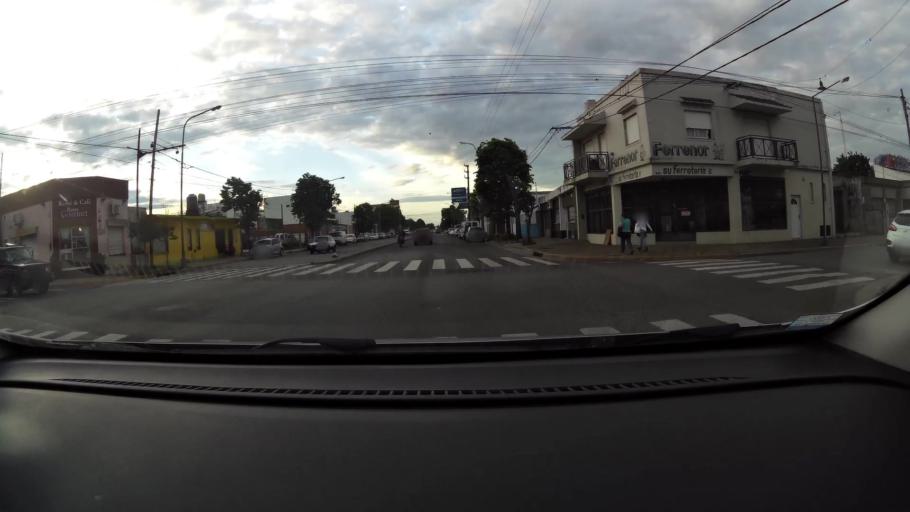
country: AR
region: Buenos Aires
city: San Nicolas de los Arroyos
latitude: -33.3313
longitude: -60.2295
